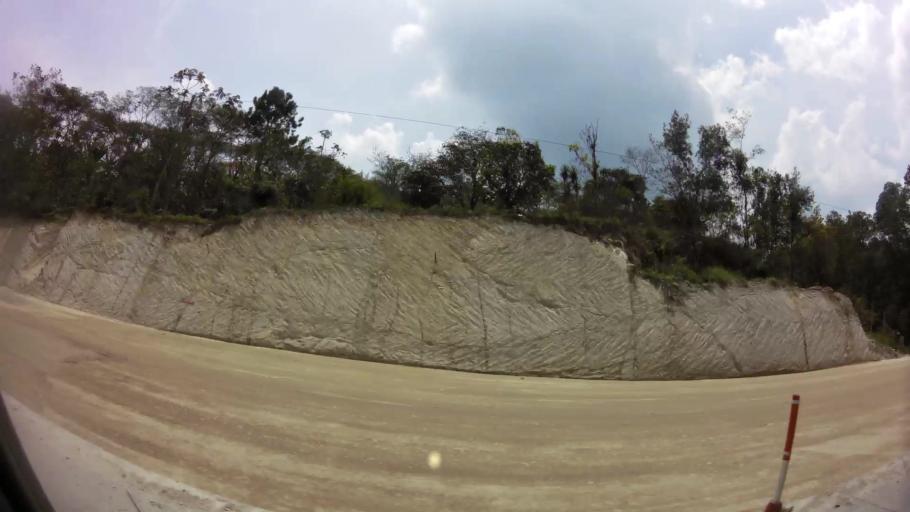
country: HN
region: Comayagua
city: El Socorro
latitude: 14.6271
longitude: -87.9111
